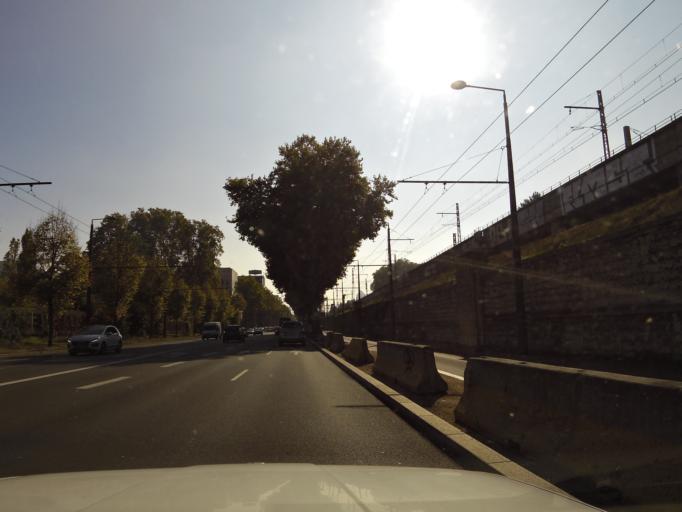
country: FR
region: Rhone-Alpes
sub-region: Departement du Rhone
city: Caluire-et-Cuire
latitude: 45.7810
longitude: 4.8597
